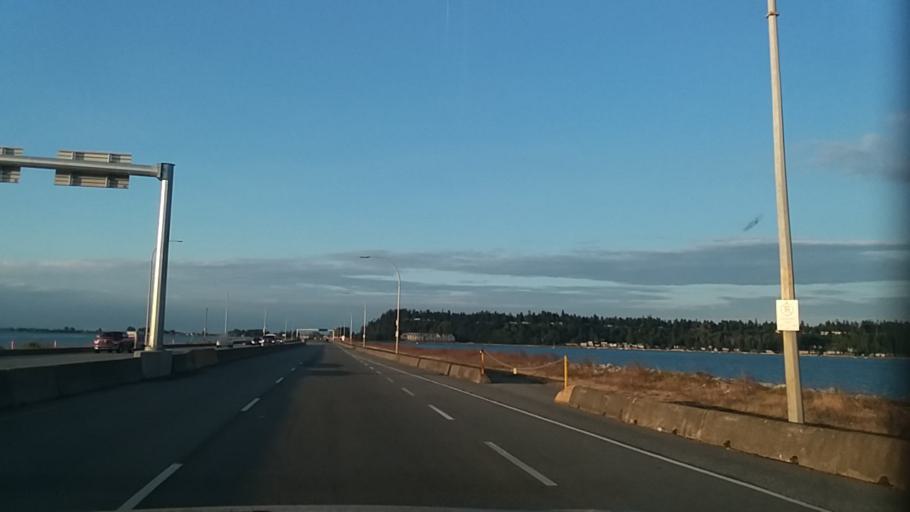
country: US
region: Washington
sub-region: Whatcom County
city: Point Roberts
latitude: 49.0126
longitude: -123.1215
